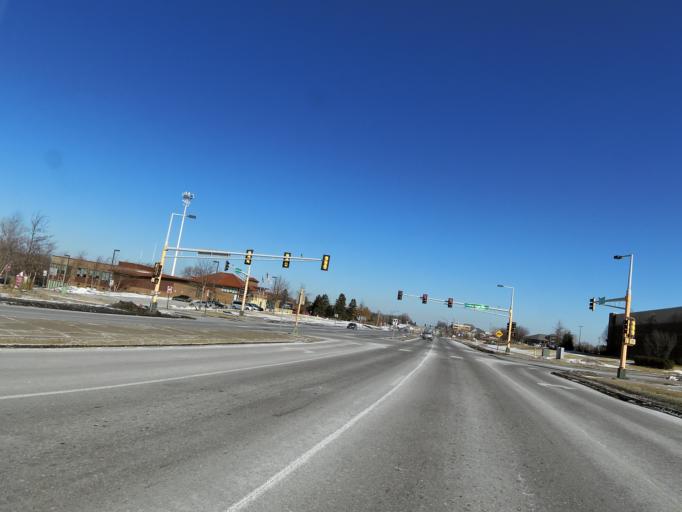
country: US
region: Minnesota
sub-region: Washington County
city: Woodbury
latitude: 44.9171
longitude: -92.9338
